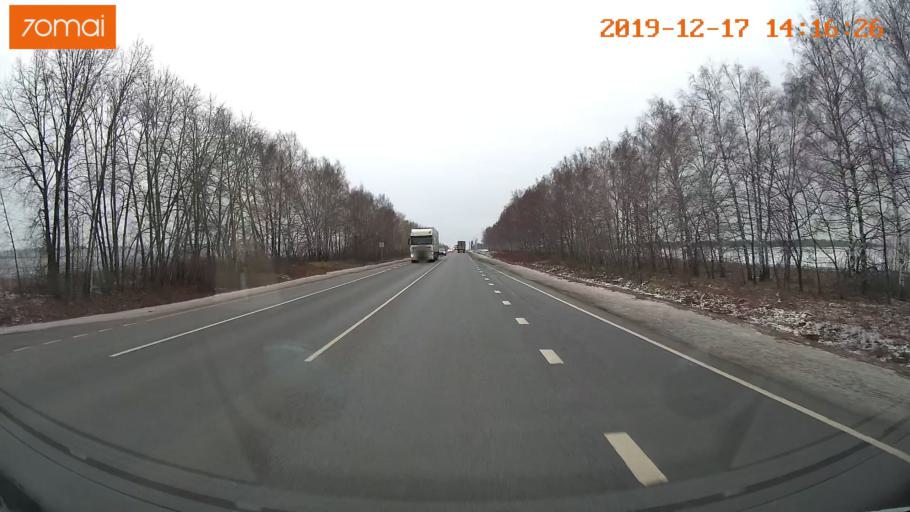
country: RU
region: Rjazan
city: Zakharovo
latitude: 54.4779
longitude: 39.4644
